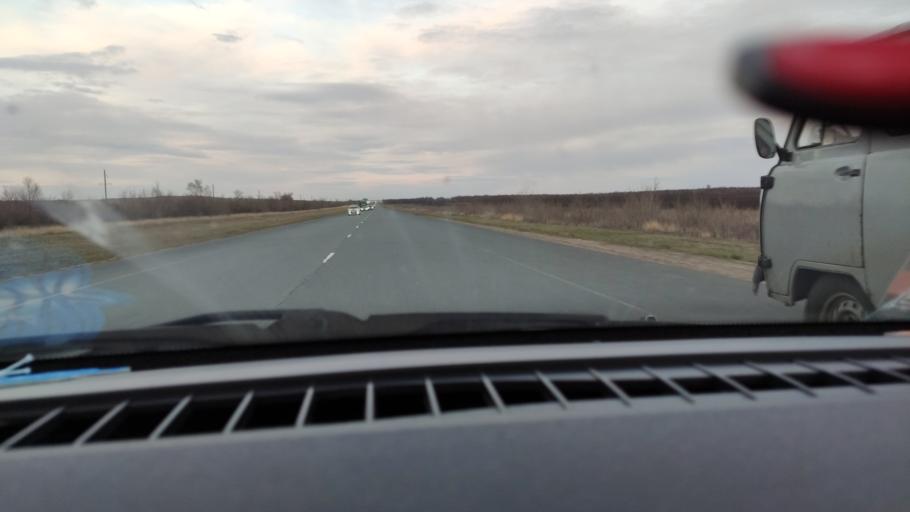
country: RU
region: Saratov
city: Yelshanka
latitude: 51.8283
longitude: 46.2601
